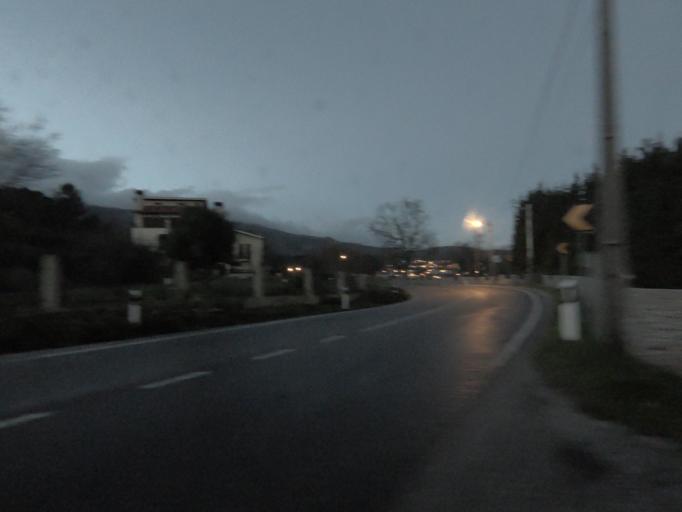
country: PT
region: Vila Real
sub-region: Vila Real
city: Vila Real
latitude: 41.3488
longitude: -7.7213
